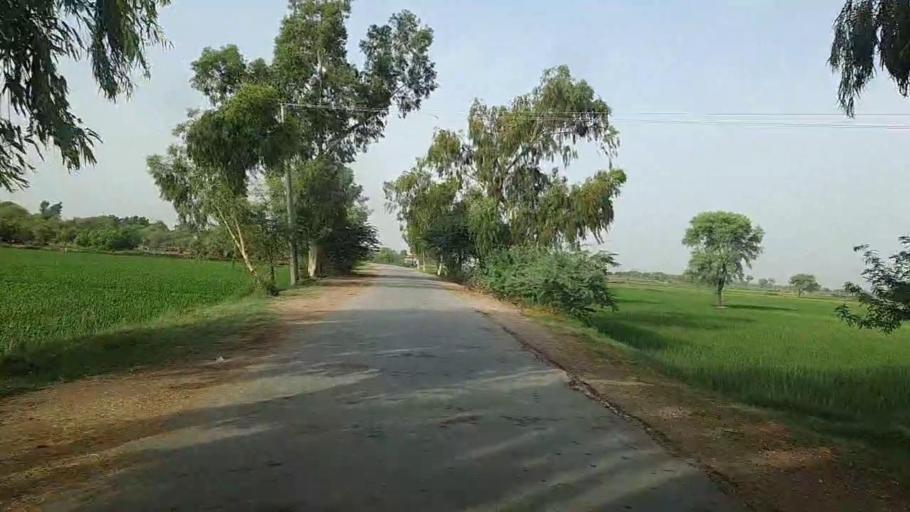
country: PK
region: Sindh
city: Khairpur Nathan Shah
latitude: 27.1203
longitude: 67.7889
